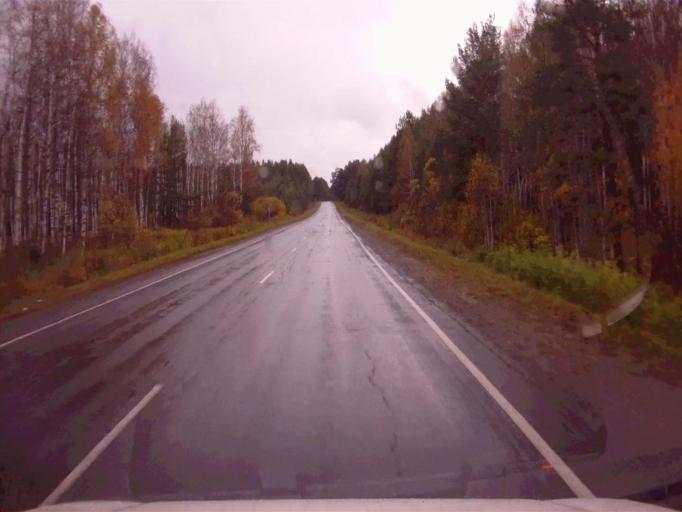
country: RU
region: Chelyabinsk
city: Verkhniy Ufaley
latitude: 56.0185
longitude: 60.3059
